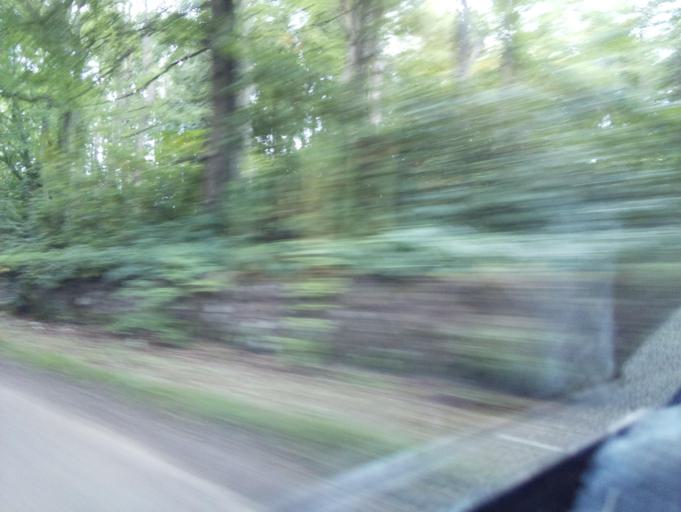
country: GB
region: Scotland
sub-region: Fife
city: Saint Andrews
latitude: 56.2925
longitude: -2.7954
